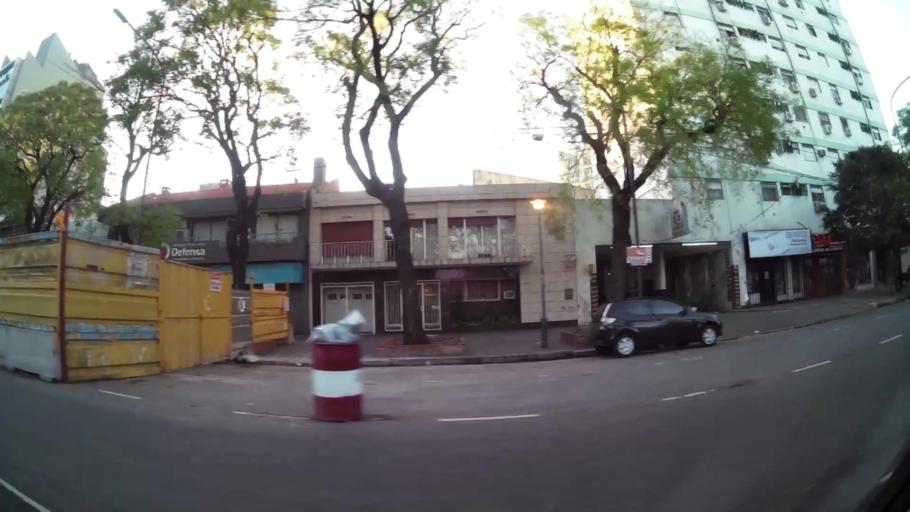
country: AR
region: Buenos Aires F.D.
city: Buenos Aires
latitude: -34.6390
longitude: -58.4115
